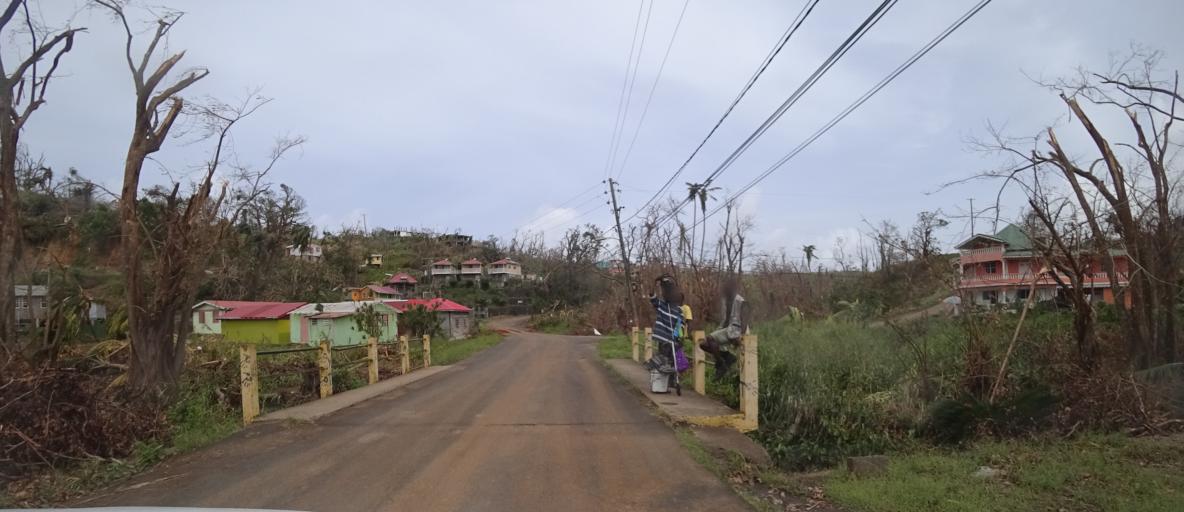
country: DM
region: Saint Andrew
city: Calibishie
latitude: 15.5935
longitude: -61.3457
